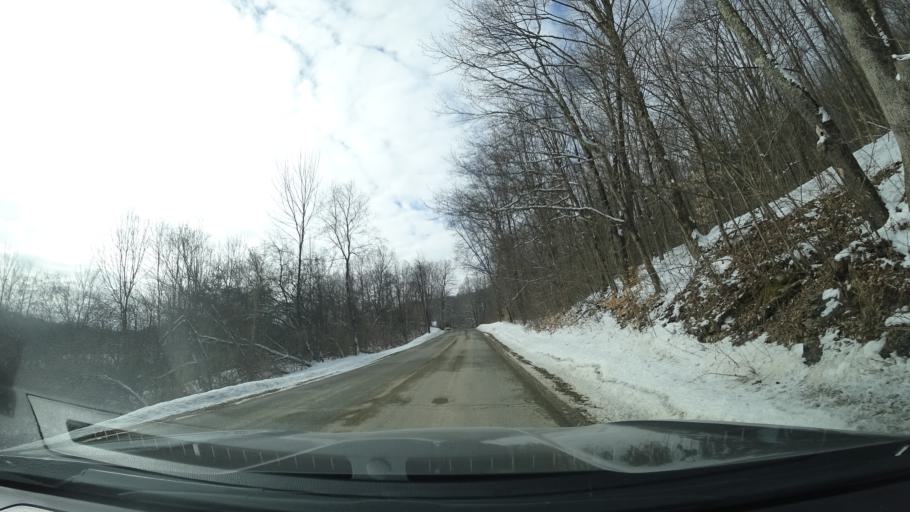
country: US
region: New York
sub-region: Washington County
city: Greenwich
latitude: 43.2181
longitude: -73.3558
